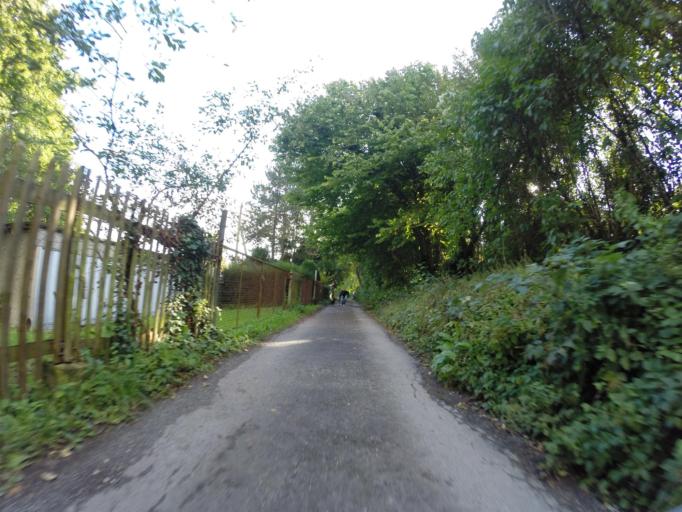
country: DE
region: Thuringia
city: Jena
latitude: 50.9428
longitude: 11.5867
